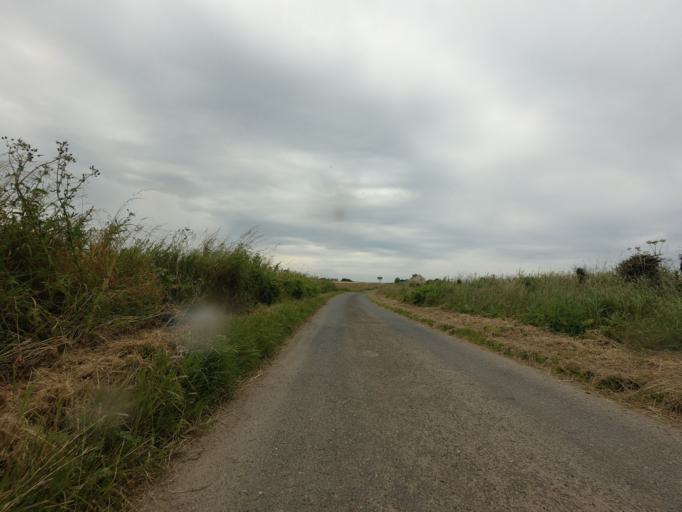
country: GB
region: Scotland
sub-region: Aberdeenshire
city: Portsoy
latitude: 57.6770
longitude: -2.6665
